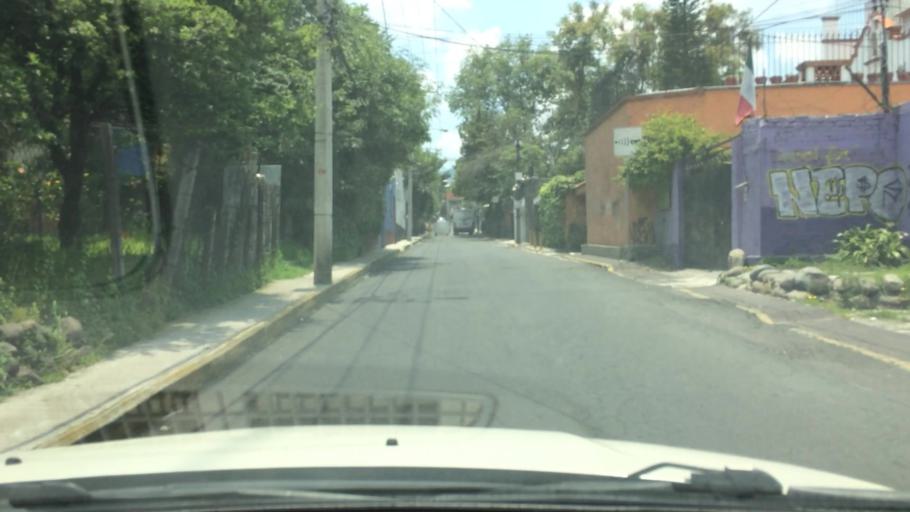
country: MX
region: Mexico City
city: Magdalena Contreras
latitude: 19.3248
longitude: -99.2251
